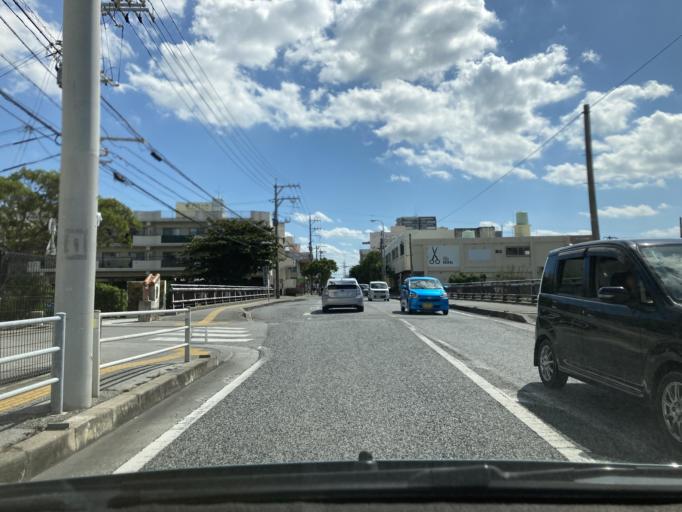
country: JP
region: Okinawa
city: Tomigusuku
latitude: 26.1952
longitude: 127.7054
